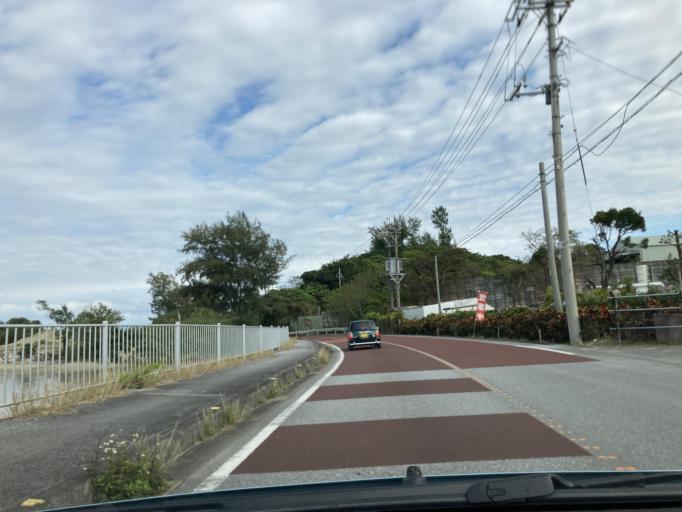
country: JP
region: Okinawa
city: Nago
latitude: 26.6465
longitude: 127.9893
